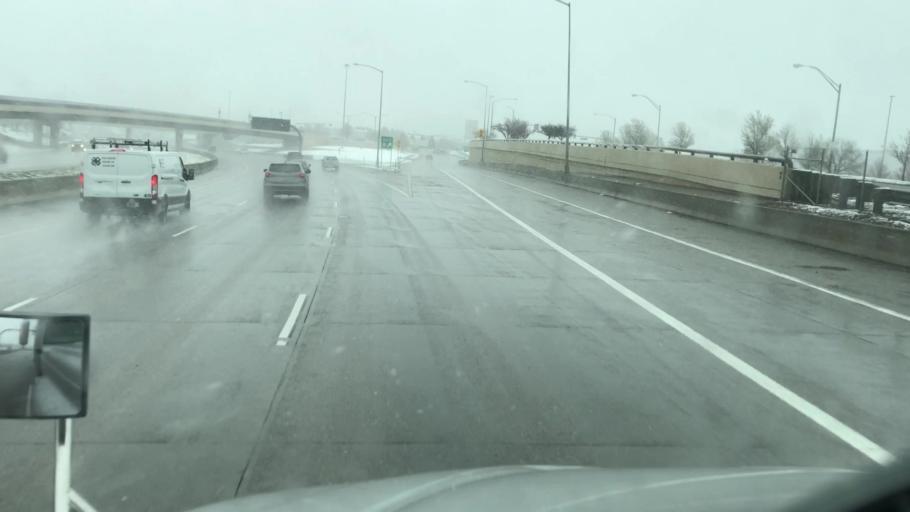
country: US
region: Colorado
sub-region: Adams County
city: Aurora
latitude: 39.7080
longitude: -104.8270
